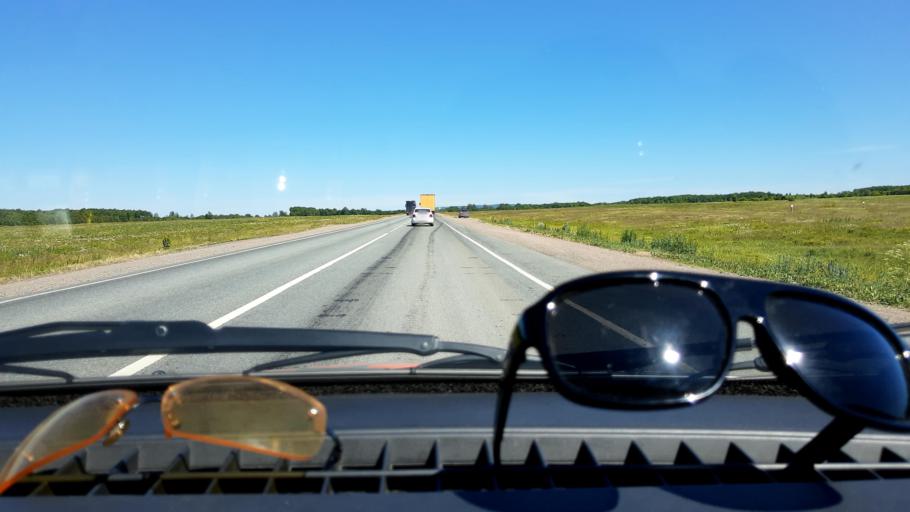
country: RU
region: Bashkortostan
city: Kudeyevskiy
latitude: 54.8172
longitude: 56.8079
